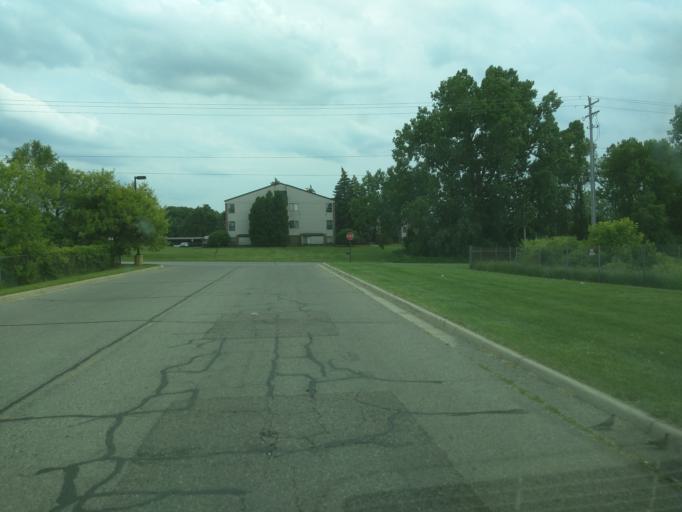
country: US
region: Michigan
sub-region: Eaton County
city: Waverly
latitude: 42.7379
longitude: -84.6263
